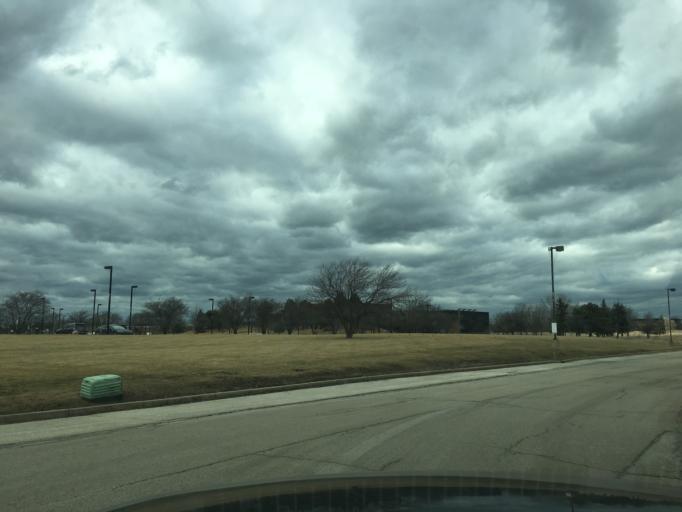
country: US
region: Illinois
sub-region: Cook County
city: Hoffman Estates
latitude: 42.0641
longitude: -88.0542
